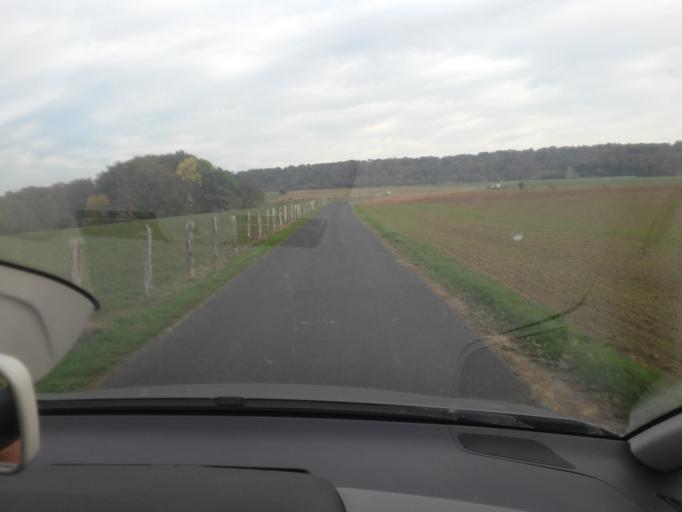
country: BE
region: Wallonia
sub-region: Province du Luxembourg
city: Attert
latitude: 49.7297
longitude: 5.7624
